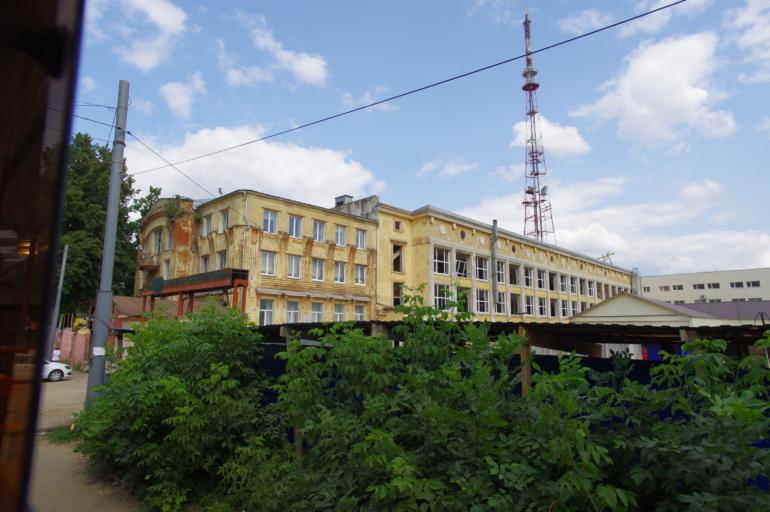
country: RU
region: Nizjnij Novgorod
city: Nizhniy Novgorod
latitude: 56.3071
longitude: 43.9878
